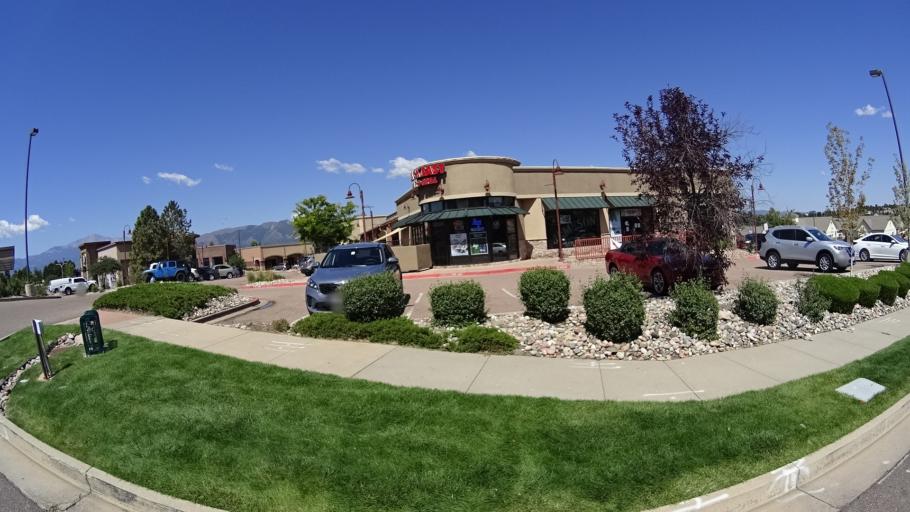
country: US
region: Colorado
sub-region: El Paso County
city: Air Force Academy
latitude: 38.9677
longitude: -104.7818
